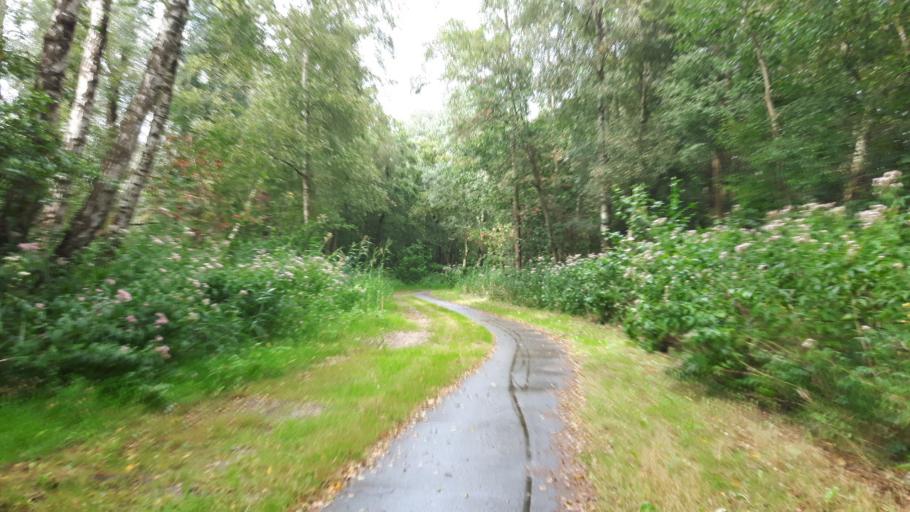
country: NL
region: Overijssel
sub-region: Gemeente Steenwijkerland
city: Blokzijl
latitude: 52.7632
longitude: 5.9589
